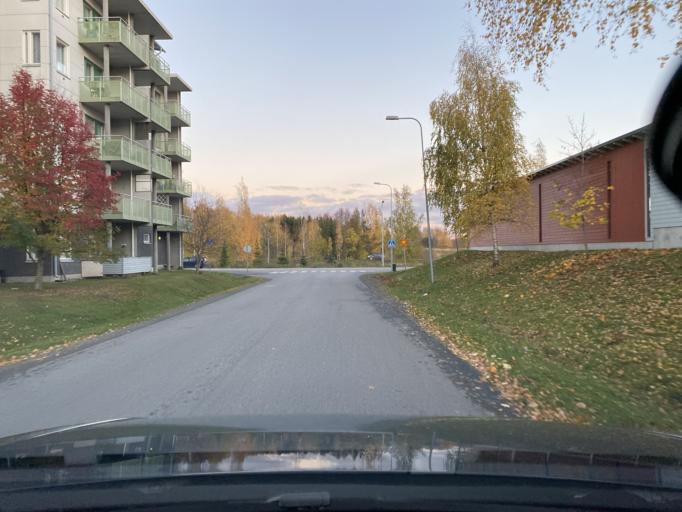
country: FI
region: Pirkanmaa
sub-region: Tampere
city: Lempaeaelae
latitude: 61.3165
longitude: 23.7594
